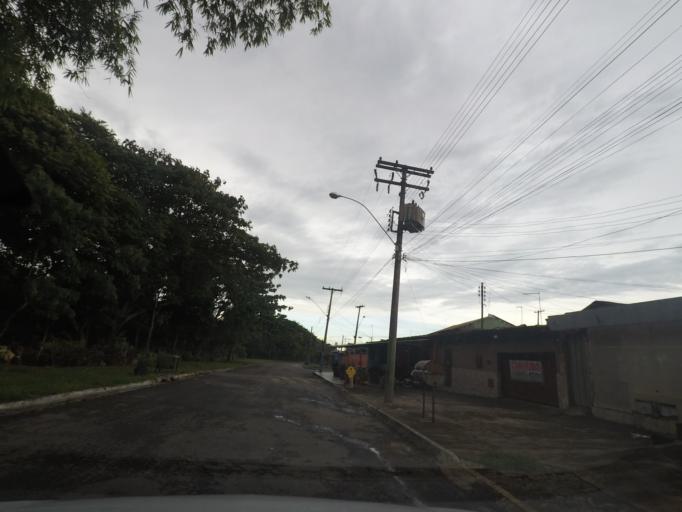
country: BR
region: Goias
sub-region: Goiania
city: Goiania
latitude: -16.7247
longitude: -49.2438
